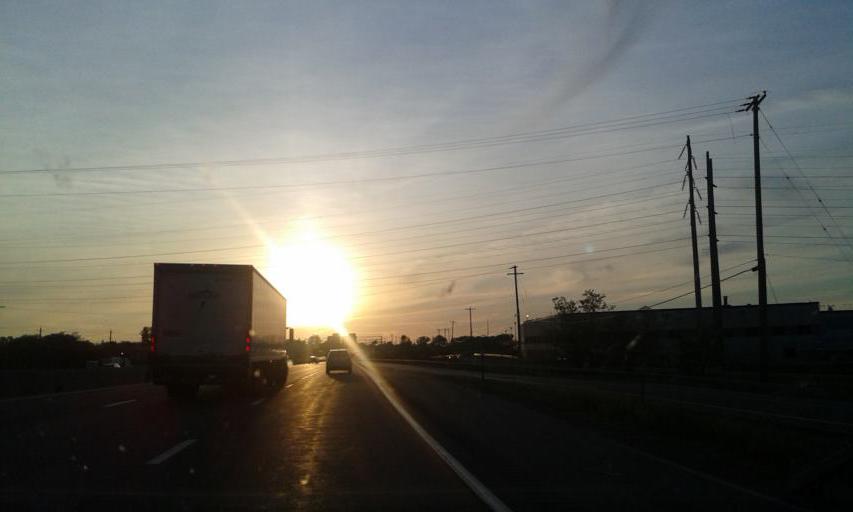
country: US
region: New York
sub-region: Onondaga County
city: Lakeland
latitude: 43.1072
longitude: -76.2552
